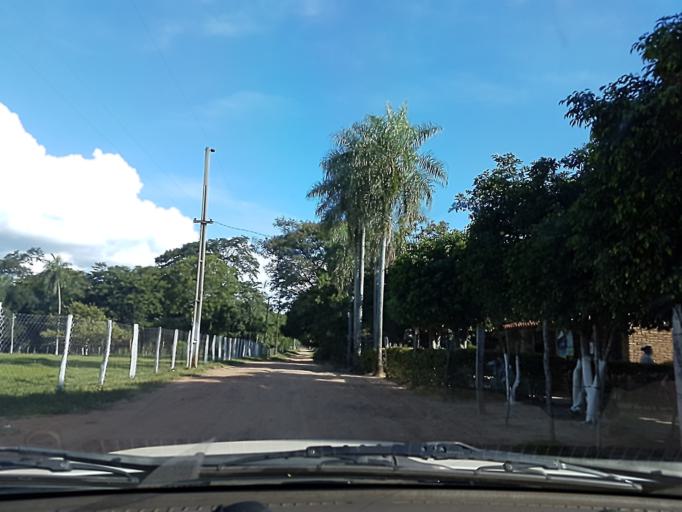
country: PY
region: Cordillera
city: Arroyos y Esteros
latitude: -24.9813
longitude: -57.1991
